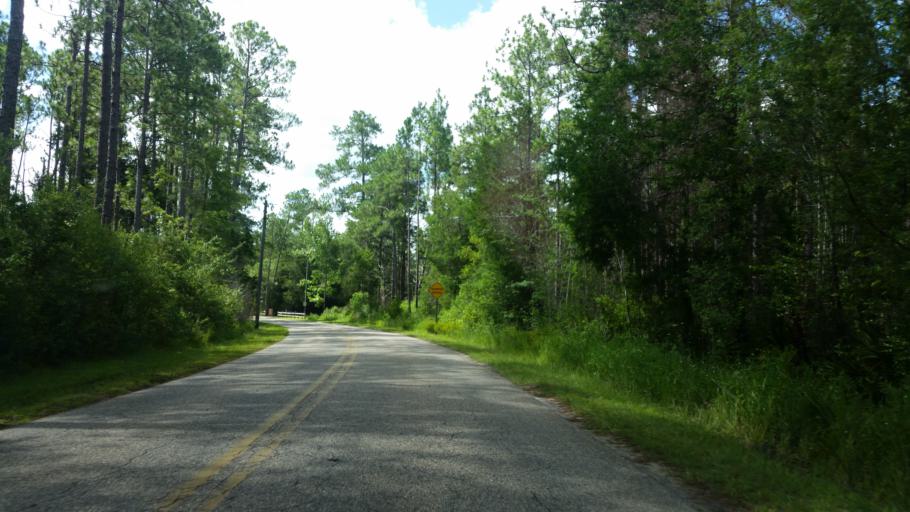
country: US
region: Florida
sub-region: Santa Rosa County
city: East Milton
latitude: 30.7066
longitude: -86.8831
